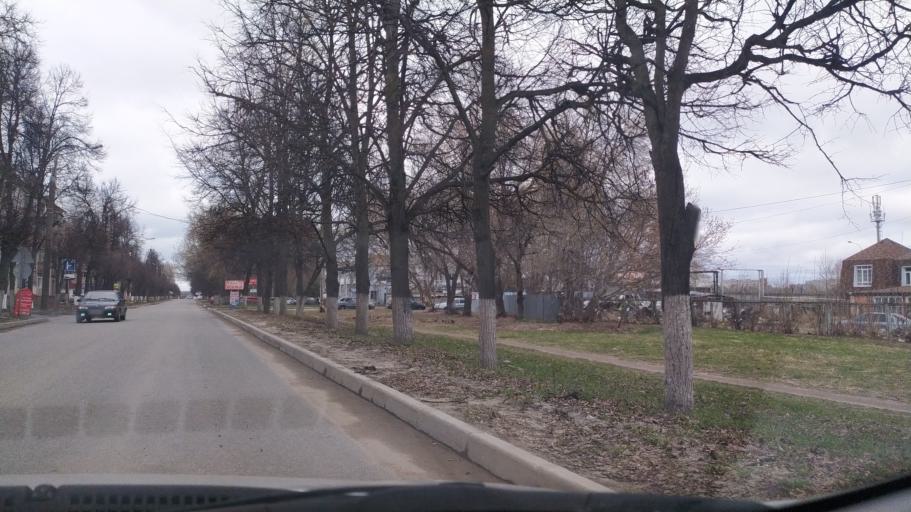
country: RU
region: Chuvashia
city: Novocheboksarsk
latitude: 56.1189
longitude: 47.5026
